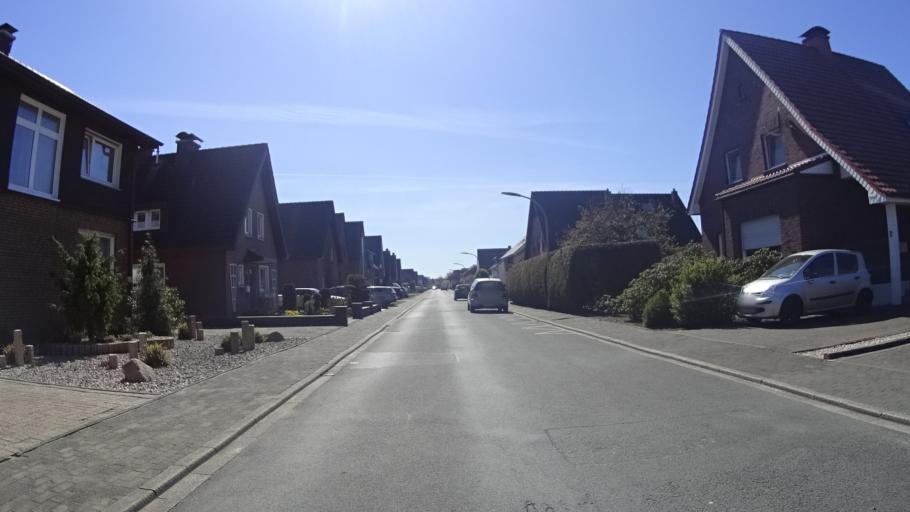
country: DE
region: North Rhine-Westphalia
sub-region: Regierungsbezirk Munster
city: Haltern
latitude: 51.7716
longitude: 7.2251
